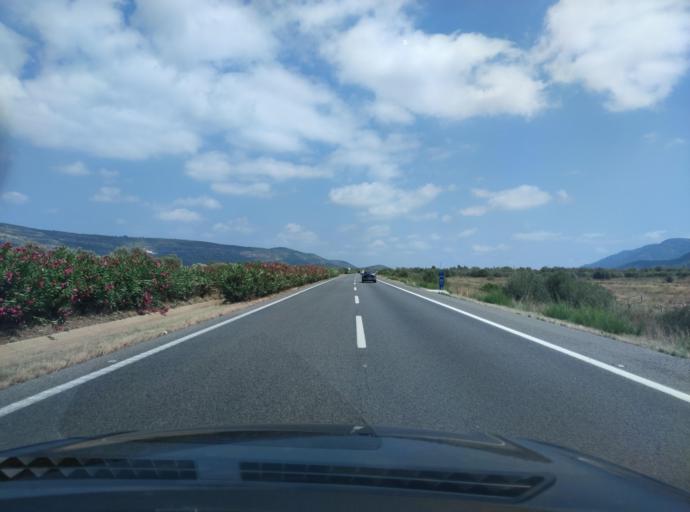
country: ES
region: Catalonia
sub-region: Provincia de Tarragona
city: Ulldecona
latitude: 40.6041
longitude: 0.4738
